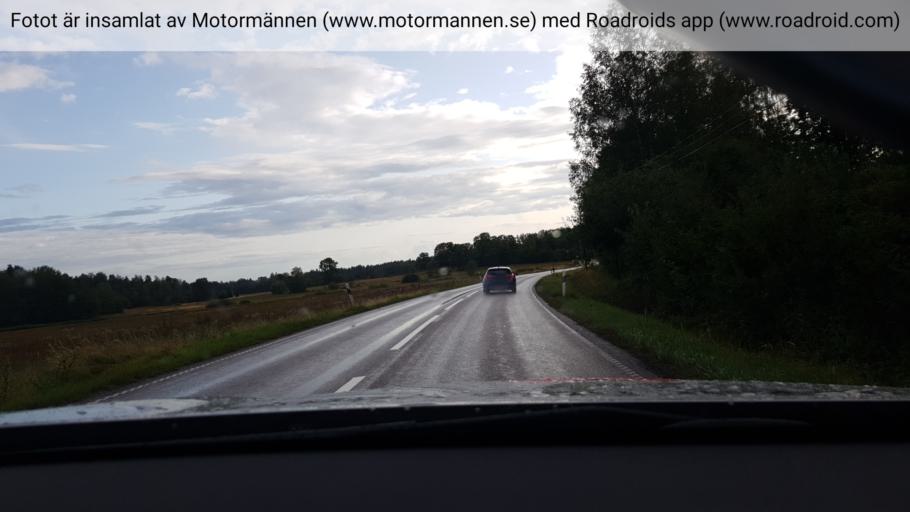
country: SE
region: Stockholm
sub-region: Norrtalje Kommun
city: Norrtalje
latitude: 59.8623
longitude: 18.6917
